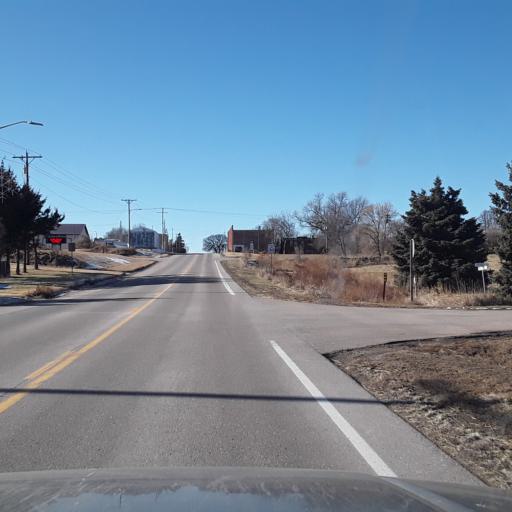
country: US
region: Nebraska
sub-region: Dawson County
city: Gothenburg
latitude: 40.7058
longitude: -100.2115
